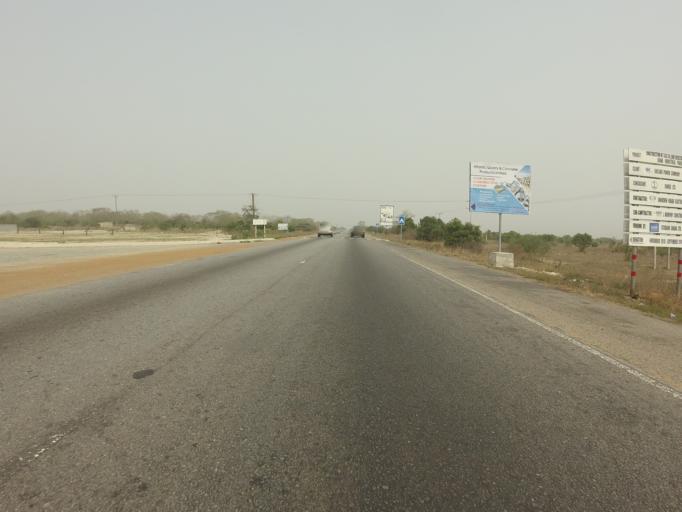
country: GH
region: Greater Accra
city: Tema
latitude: 5.8547
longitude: 0.2637
